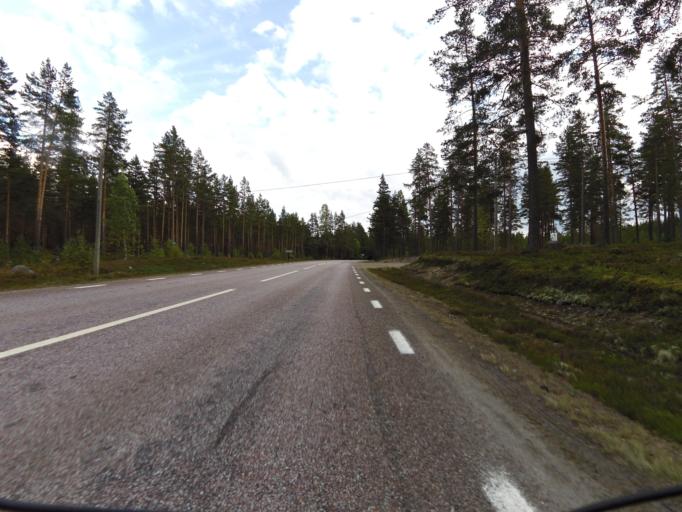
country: SE
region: Gaevleborg
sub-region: Sandvikens Kommun
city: Sandviken
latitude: 60.7192
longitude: 16.7980
